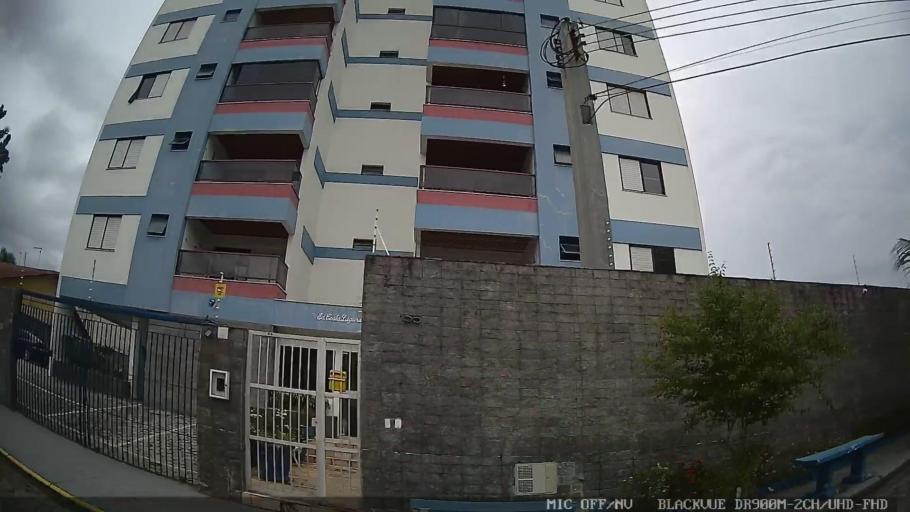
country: BR
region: Sao Paulo
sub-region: Caraguatatuba
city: Caraguatatuba
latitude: -23.6226
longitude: -45.3785
